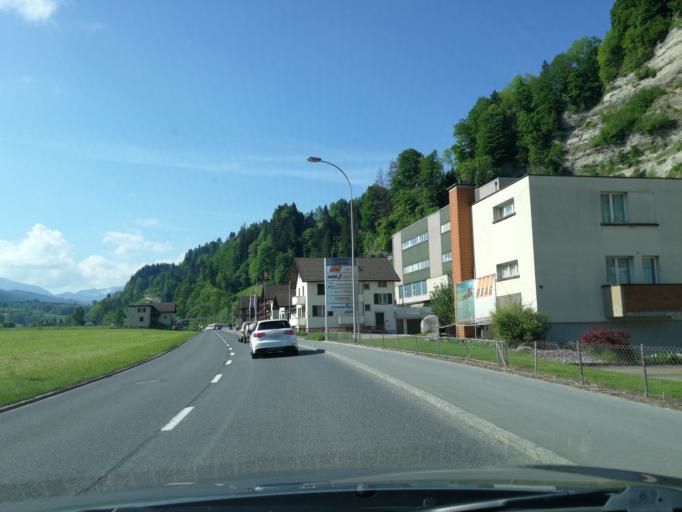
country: CH
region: Lucerne
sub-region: Entlebuch District
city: Wolhusen
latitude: 47.0504
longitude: 8.0667
